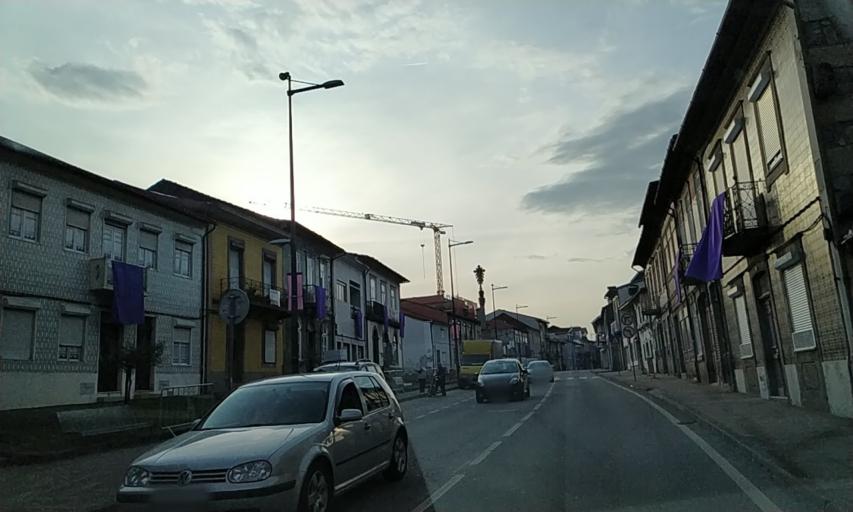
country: PT
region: Porto
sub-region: Valongo
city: Valongo
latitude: 41.1883
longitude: -8.4931
